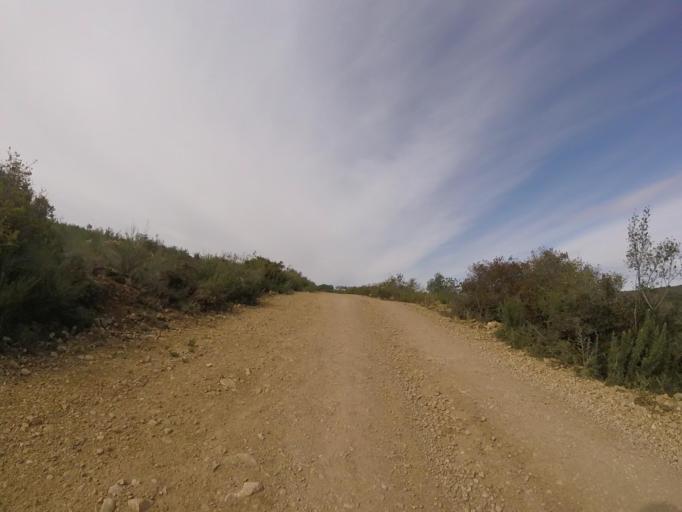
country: ES
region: Valencia
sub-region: Provincia de Castello
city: Torreblanca
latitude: 40.2028
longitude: 0.1388
